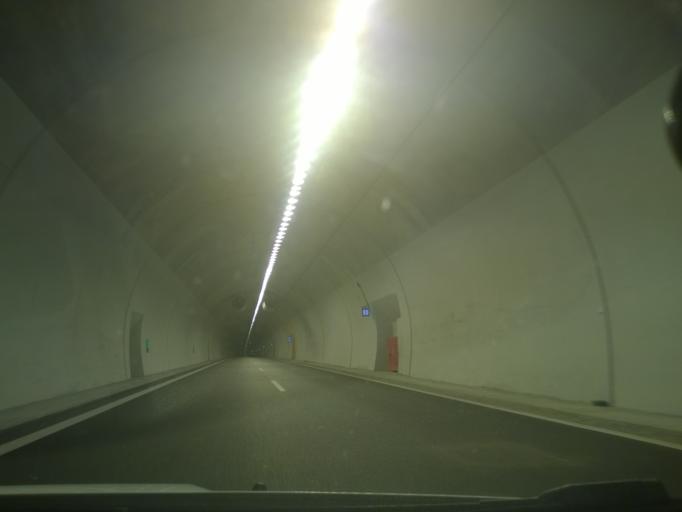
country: GR
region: West Greece
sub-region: Nomos Achaias
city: Aiyira
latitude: 38.1397
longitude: 22.3770
